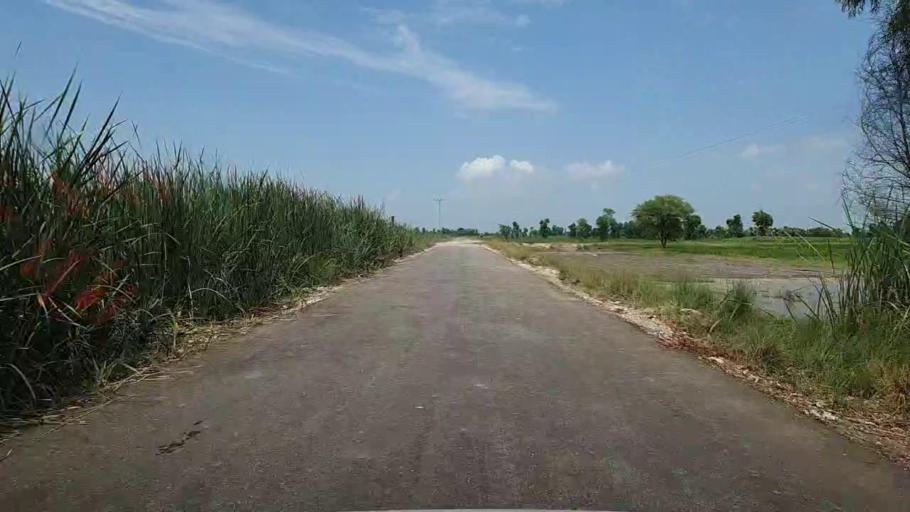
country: PK
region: Sindh
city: Bhiria
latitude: 26.9200
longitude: 68.2071
